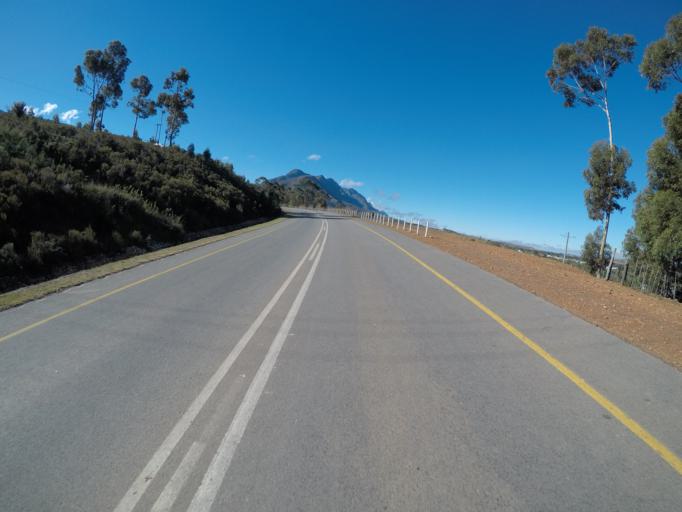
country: ZA
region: Western Cape
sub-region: Overberg District Municipality
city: Caledon
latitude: -34.0561
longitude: 19.5993
